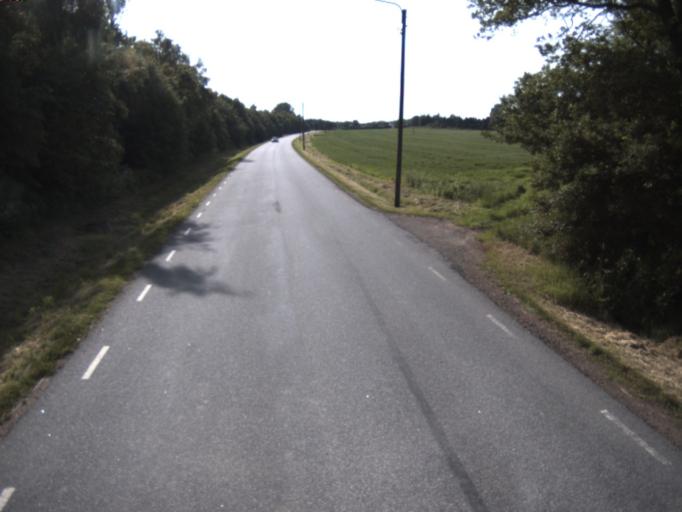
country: SE
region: Skane
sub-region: Helsingborg
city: Odakra
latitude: 56.0808
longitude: 12.7614
